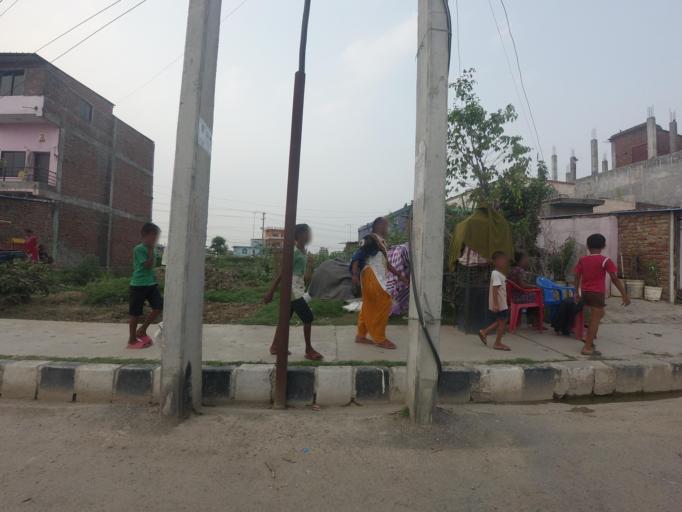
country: NP
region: Western Region
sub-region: Lumbini Zone
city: Bhairahawa
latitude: 27.5092
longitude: 83.4191
